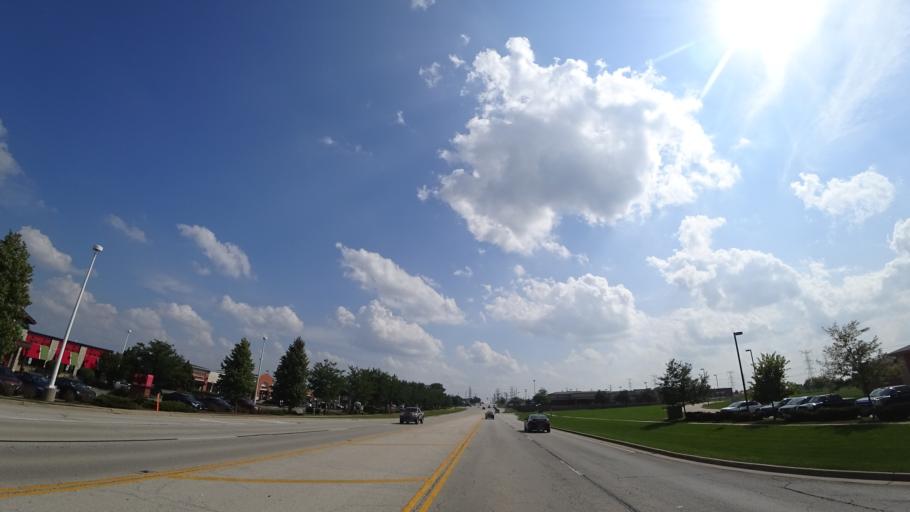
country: US
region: Illinois
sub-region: Will County
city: Goodings Grove
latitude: 41.6343
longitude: -87.9312
